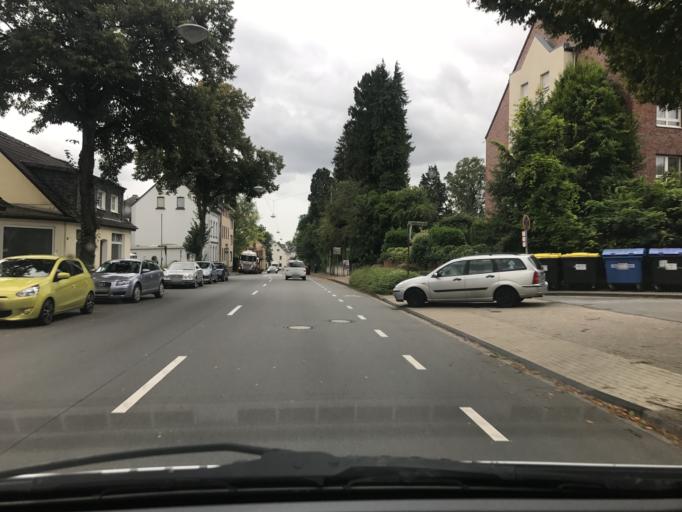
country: DE
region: North Rhine-Westphalia
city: Haan
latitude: 51.1976
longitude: 7.0158
